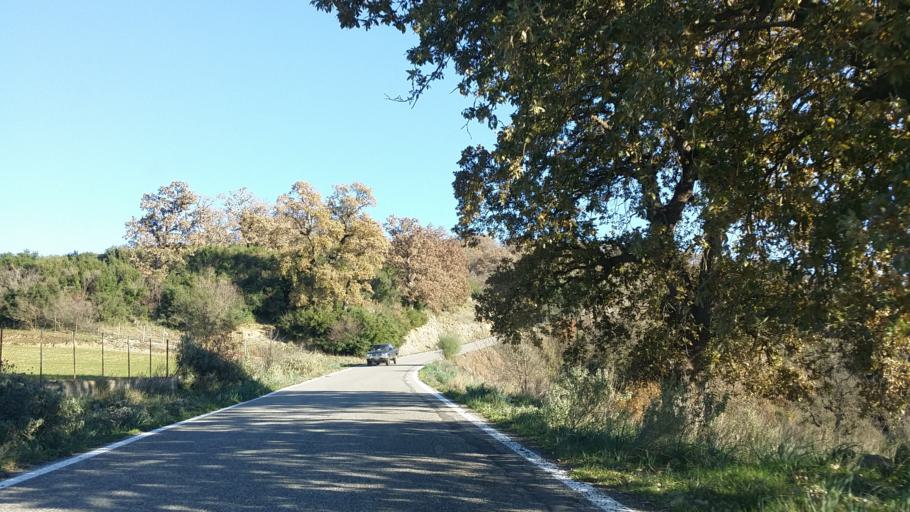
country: GR
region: West Greece
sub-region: Nomos Aitolias kai Akarnanias
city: Fitiai
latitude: 38.6386
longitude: 21.1882
